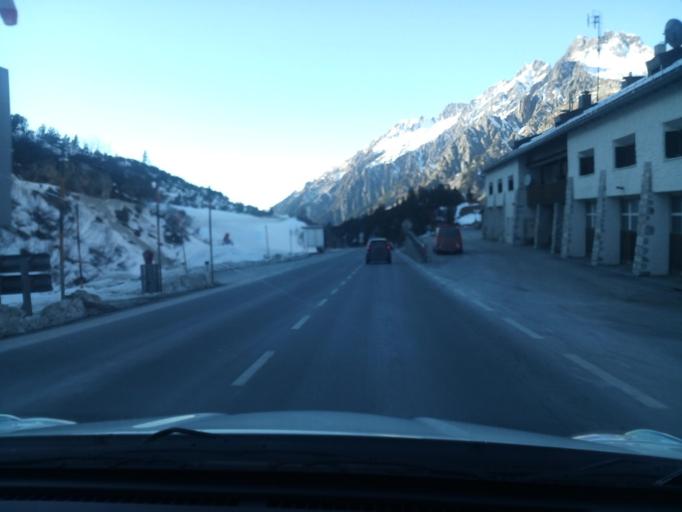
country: AT
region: Vorarlberg
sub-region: Politischer Bezirk Bludenz
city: Lech
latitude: 47.1368
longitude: 10.1788
